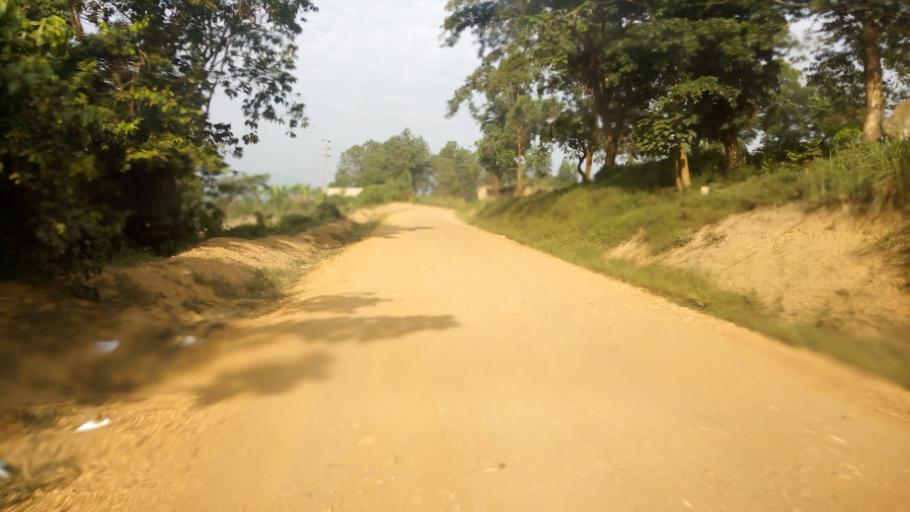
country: UG
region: Western Region
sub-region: Kanungu District
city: Ntungamo
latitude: -0.8353
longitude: 29.6709
